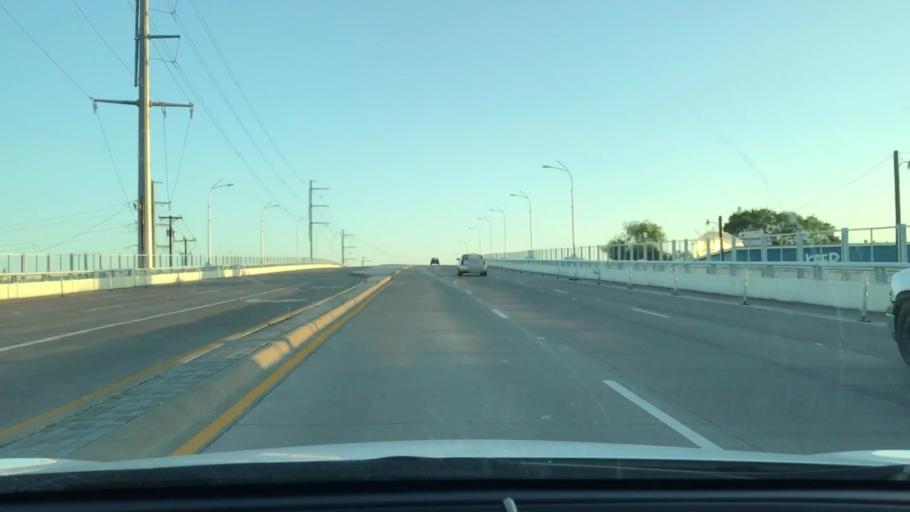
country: US
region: Texas
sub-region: Dallas County
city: Dallas
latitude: 32.7952
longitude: -96.8341
